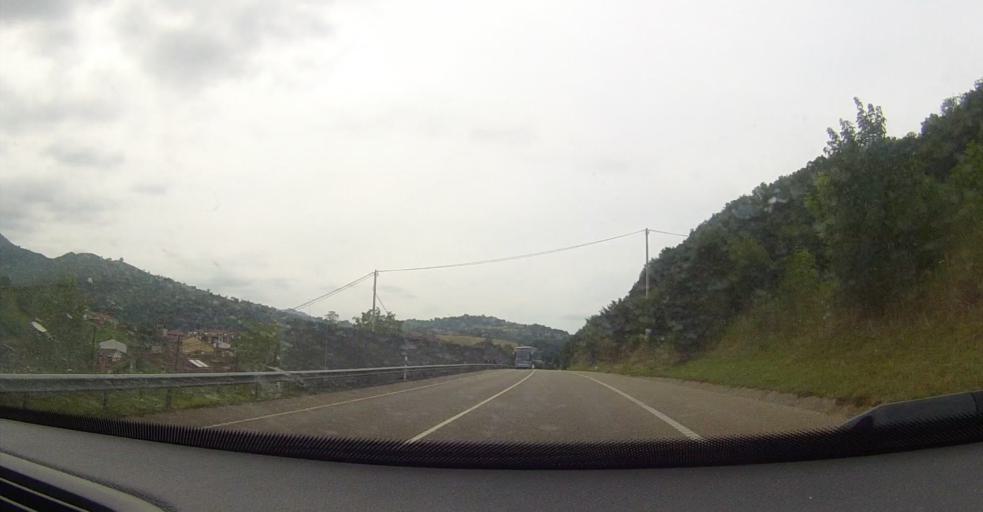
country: ES
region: Asturias
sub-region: Province of Asturias
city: Cangas de Onis
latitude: 43.3516
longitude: -5.1195
